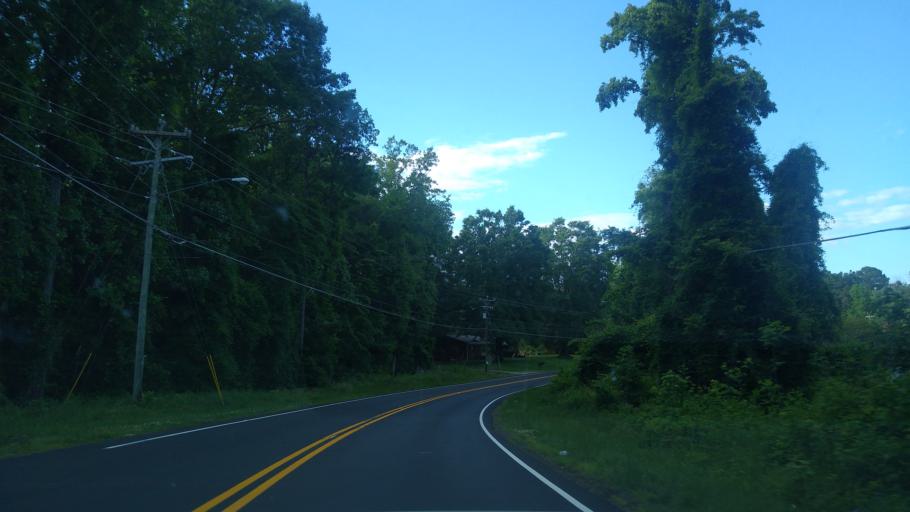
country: US
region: North Carolina
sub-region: Guilford County
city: McLeansville
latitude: 36.1593
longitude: -79.7362
